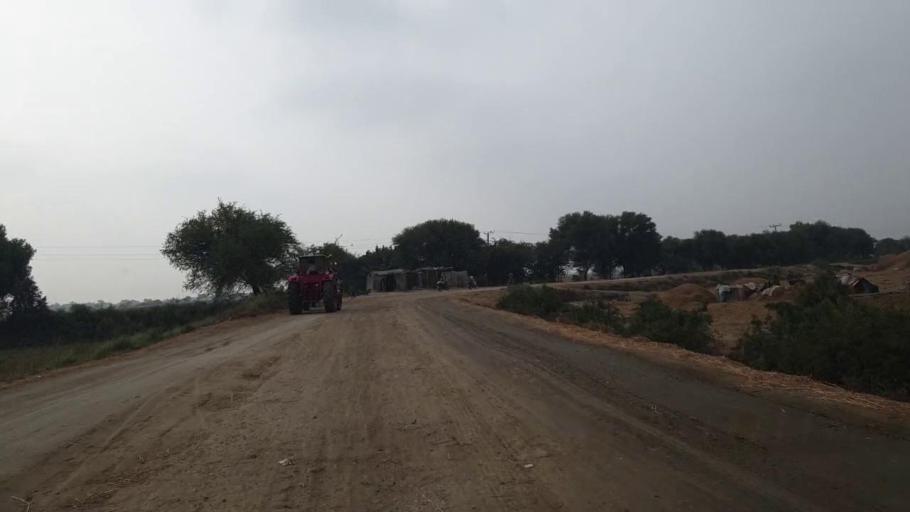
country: PK
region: Sindh
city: Kario
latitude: 24.9352
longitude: 68.5756
